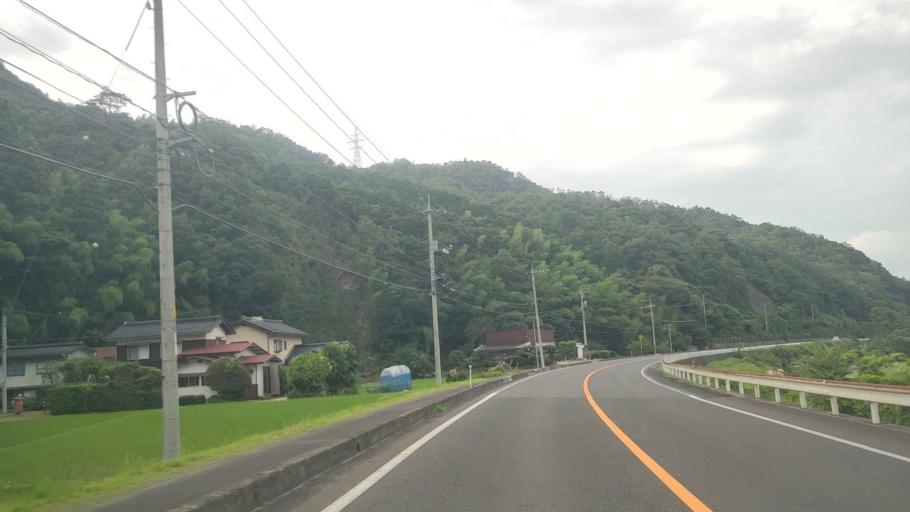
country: JP
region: Tottori
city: Kurayoshi
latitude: 35.3761
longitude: 133.8490
